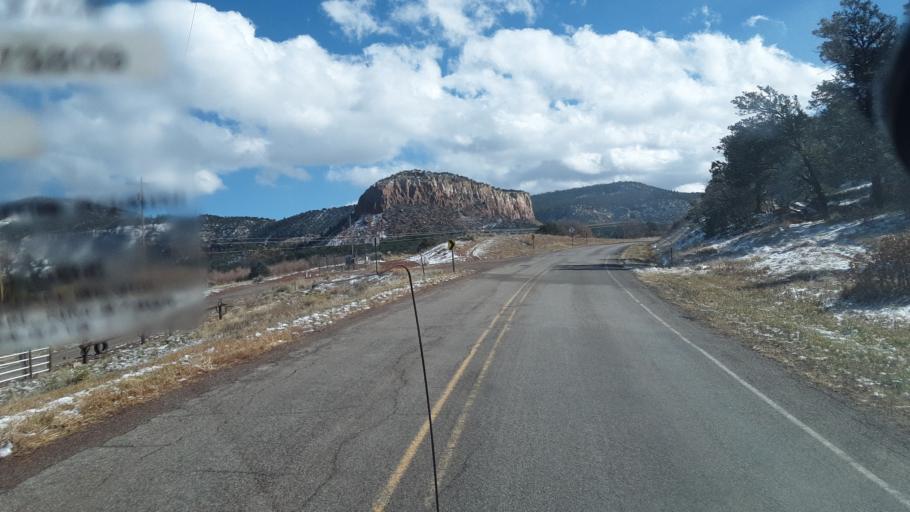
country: US
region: New Mexico
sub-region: Rio Arriba County
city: Santa Teresa
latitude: 36.2308
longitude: -106.8057
